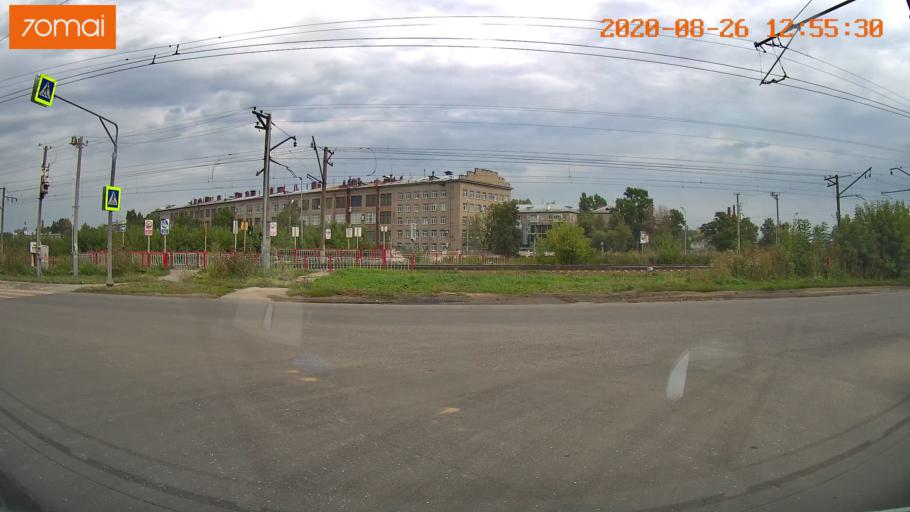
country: RU
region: Rjazan
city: Ryazan'
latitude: 54.6092
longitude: 39.7582
